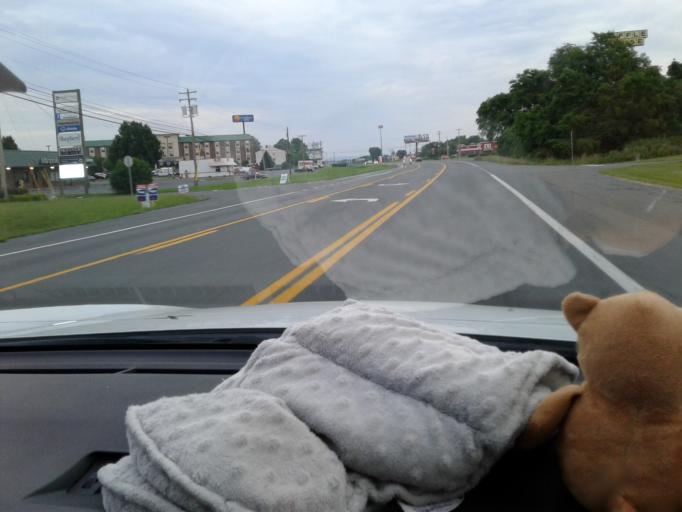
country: US
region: West Virginia
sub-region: Berkeley County
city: Martinsburg
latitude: 39.4854
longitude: -77.9578
